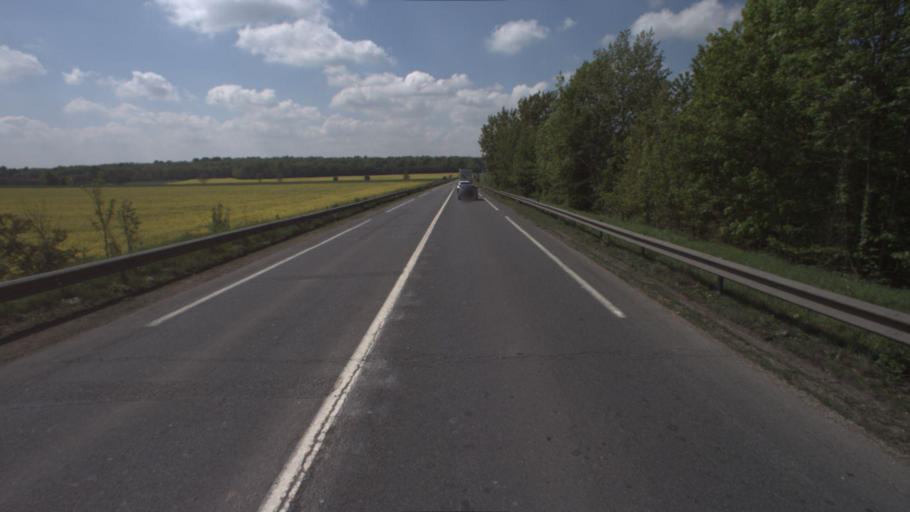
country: FR
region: Ile-de-France
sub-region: Departement de Seine-et-Marne
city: Fontenay-Tresigny
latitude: 48.7160
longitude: 2.8455
